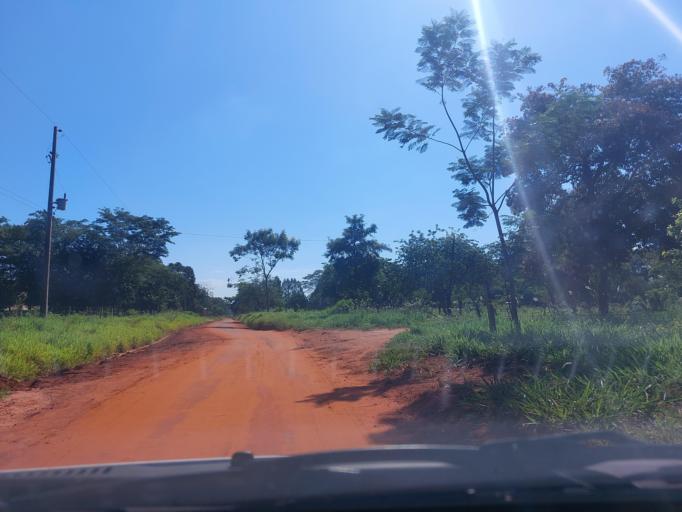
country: PY
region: San Pedro
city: Lima
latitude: -24.1502
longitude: -56.0114
